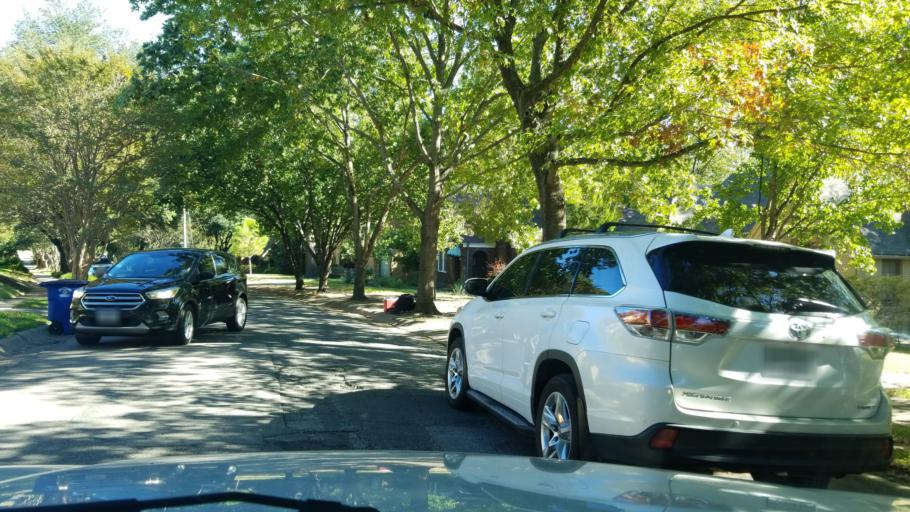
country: US
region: Texas
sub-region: Dallas County
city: Highland Park
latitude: 32.8020
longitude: -96.7430
